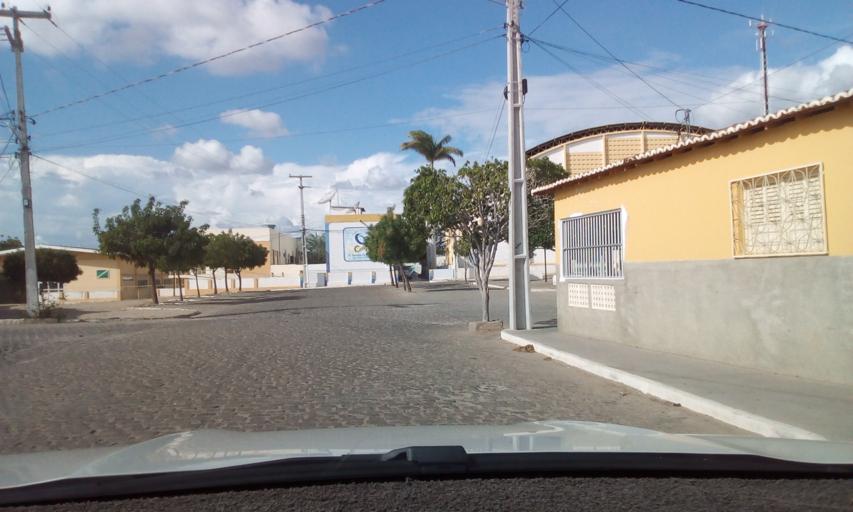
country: BR
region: Paraiba
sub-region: Picui
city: Picui
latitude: -6.5095
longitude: -36.3510
